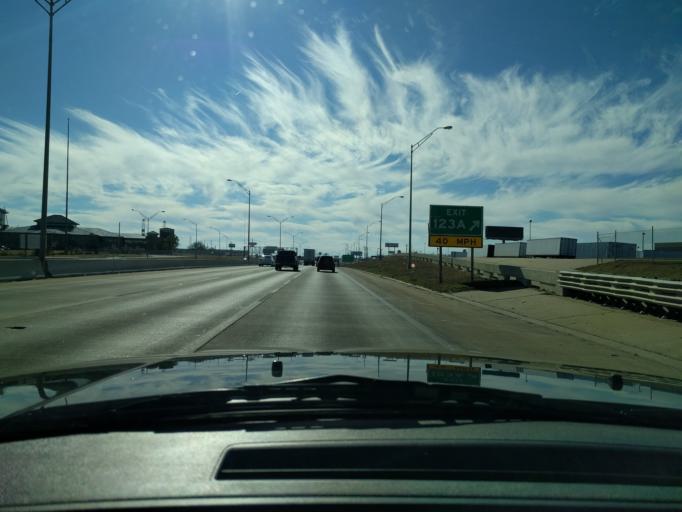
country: US
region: Oklahoma
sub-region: Oklahoma County
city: Del City
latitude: 35.4172
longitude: -97.4899
